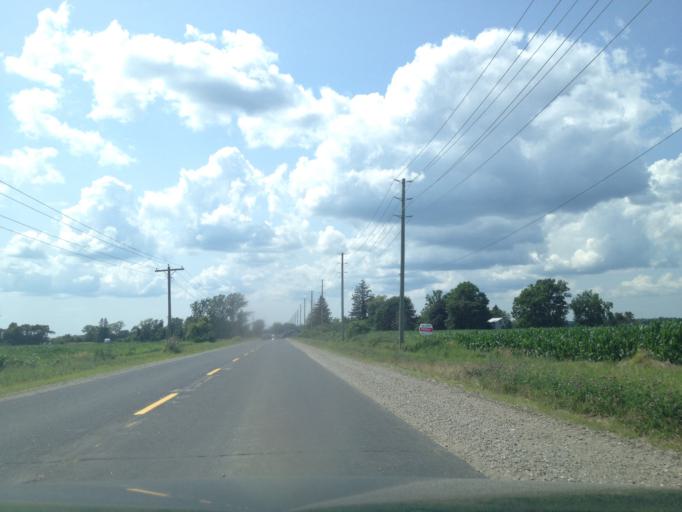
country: CA
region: Ontario
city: Aylmer
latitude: 42.6708
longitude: -80.8475
